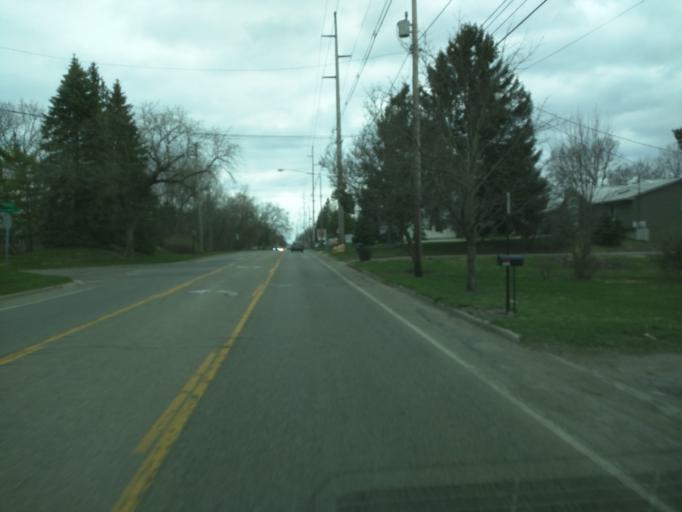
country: US
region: Michigan
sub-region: Ingham County
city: Lansing
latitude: 42.6959
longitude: -84.5234
